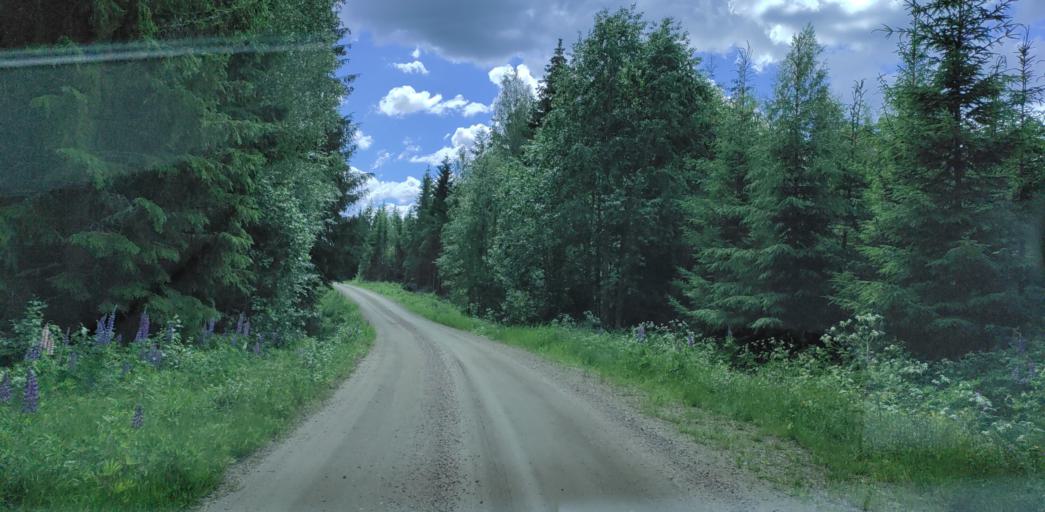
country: SE
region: Vaermland
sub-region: Hagfors Kommun
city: Ekshaerad
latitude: 60.0806
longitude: 13.3134
